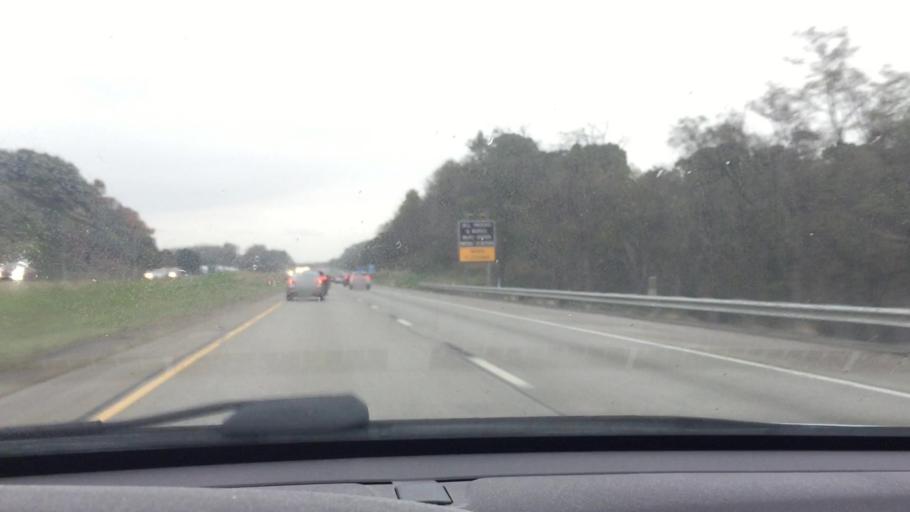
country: US
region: Pennsylvania
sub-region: Allegheny County
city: Bridgeville
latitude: 40.3244
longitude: -80.1434
